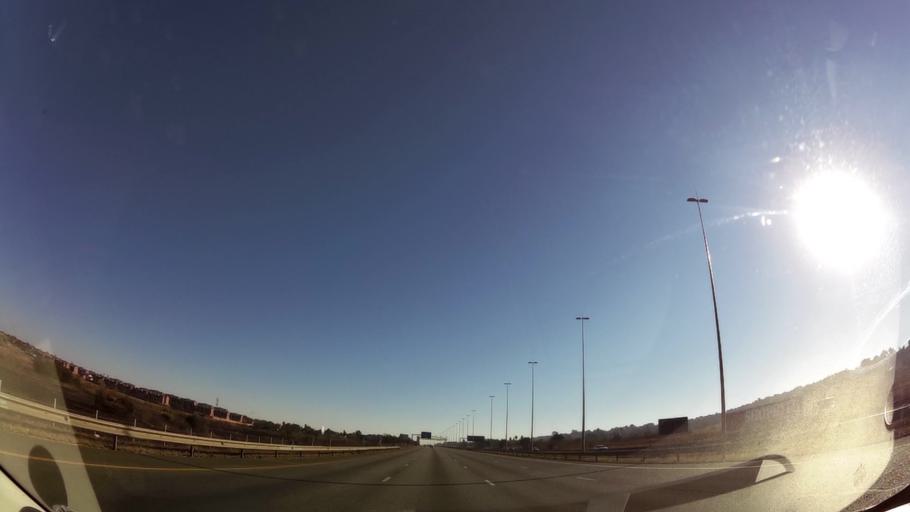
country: ZA
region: Gauteng
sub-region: City of Tshwane Metropolitan Municipality
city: Centurion
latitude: -25.8553
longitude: 28.2521
